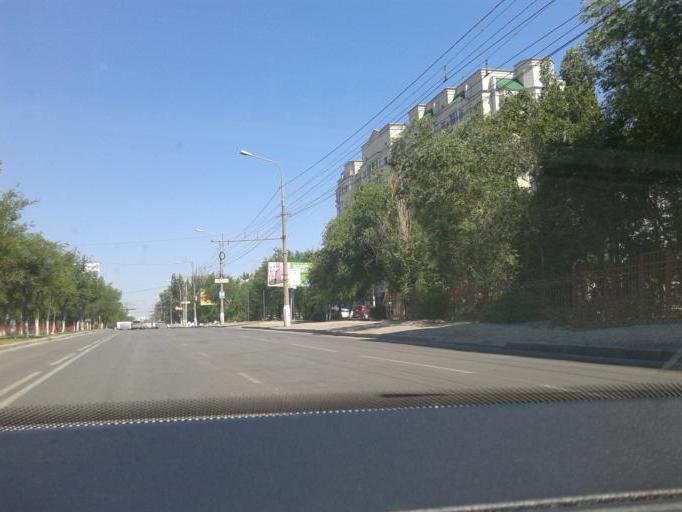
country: RU
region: Volgograd
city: Volgograd
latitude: 48.7330
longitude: 44.4962
